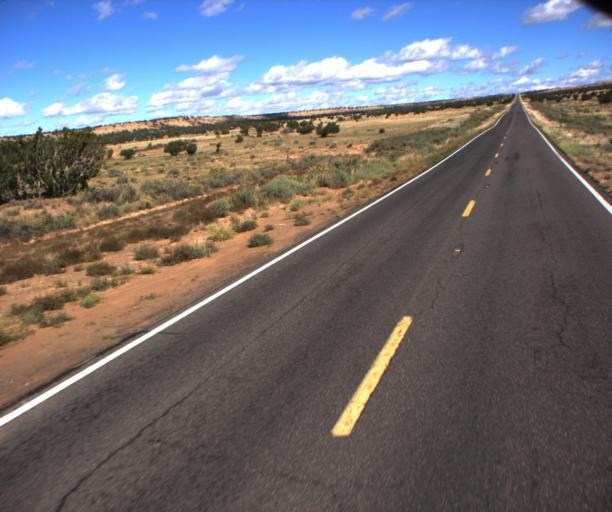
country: US
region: Arizona
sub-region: Apache County
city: Saint Johns
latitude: 34.7952
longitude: -109.2381
